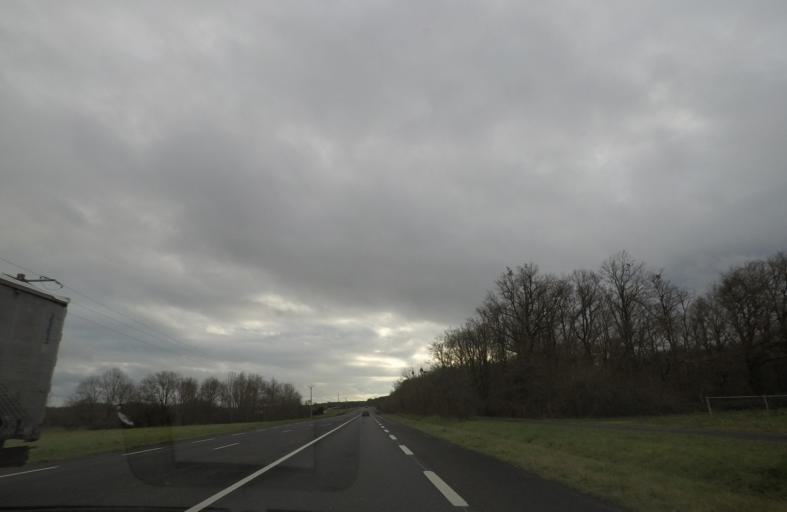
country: FR
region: Centre
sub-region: Departement du Loir-et-Cher
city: Soings-en-Sologne
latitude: 47.4459
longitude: 1.5404
